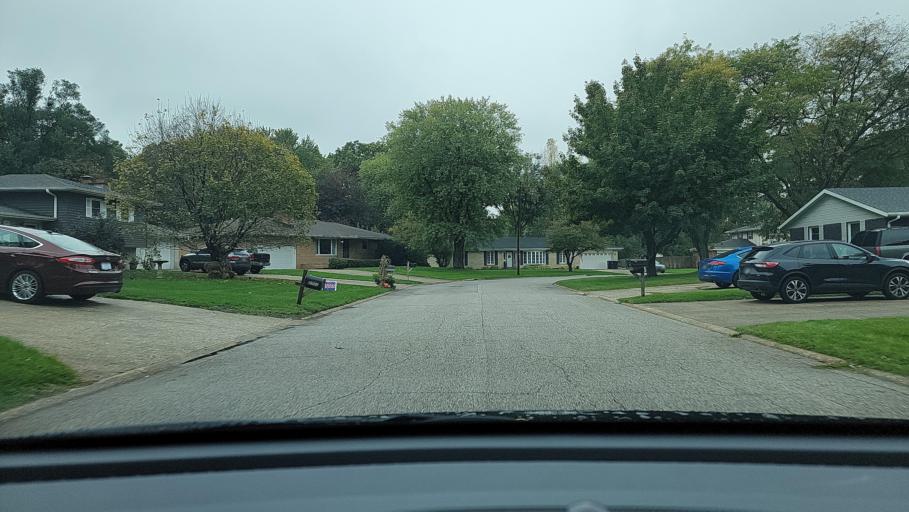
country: US
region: Indiana
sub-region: Porter County
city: Portage
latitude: 41.5732
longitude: -87.1787
